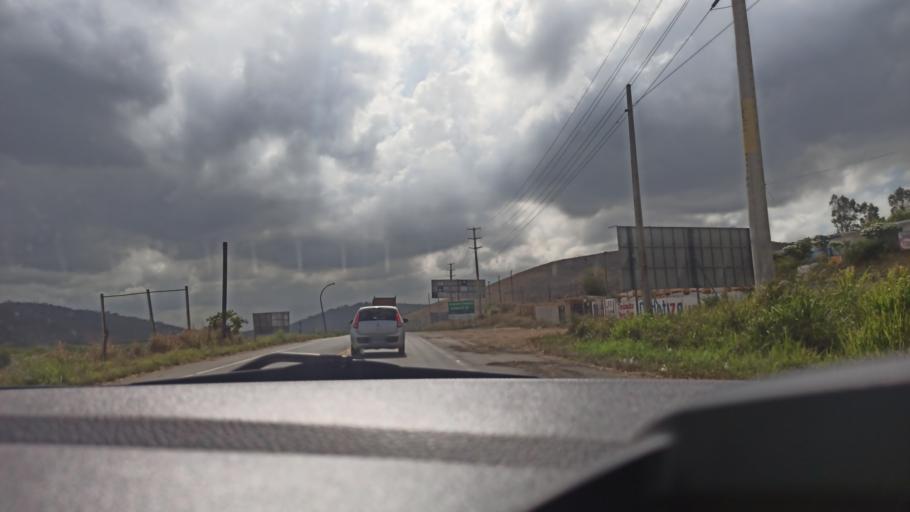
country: BR
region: Pernambuco
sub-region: Timbauba
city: Timbauba
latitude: -7.5213
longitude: -35.3042
